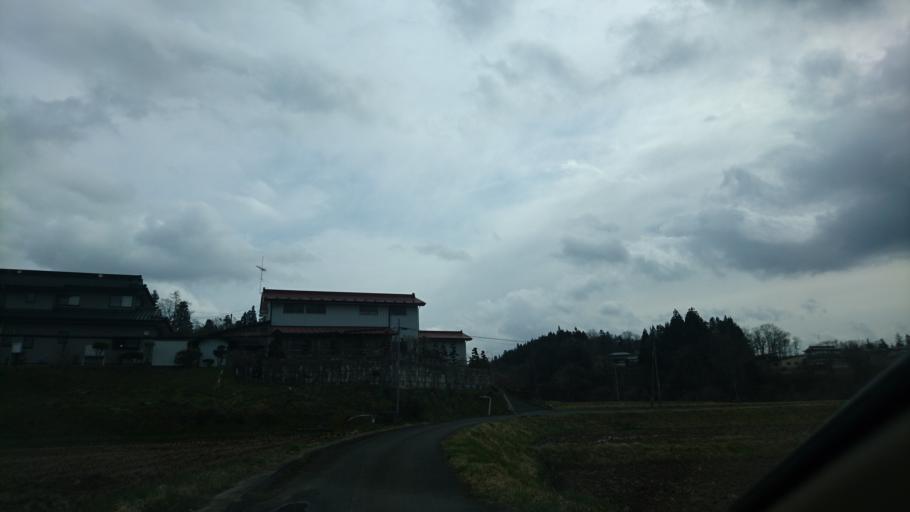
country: JP
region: Iwate
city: Ichinoseki
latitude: 38.8998
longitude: 141.1736
